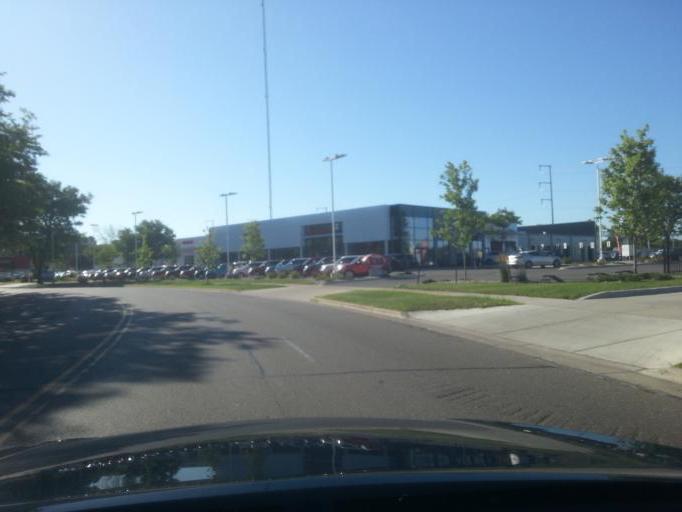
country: US
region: Wisconsin
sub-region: Dane County
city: Middleton
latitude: 43.0552
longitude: -89.4944
